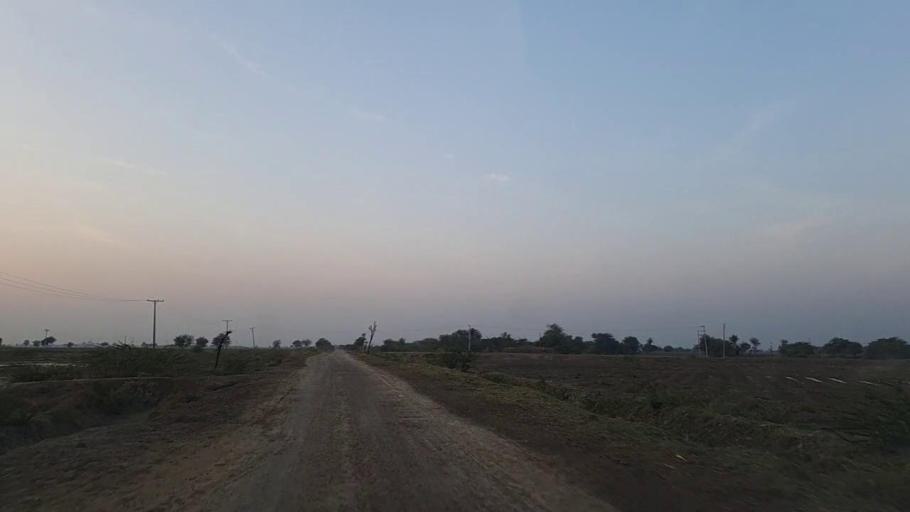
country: PK
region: Sindh
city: Naukot
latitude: 24.9785
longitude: 69.4295
